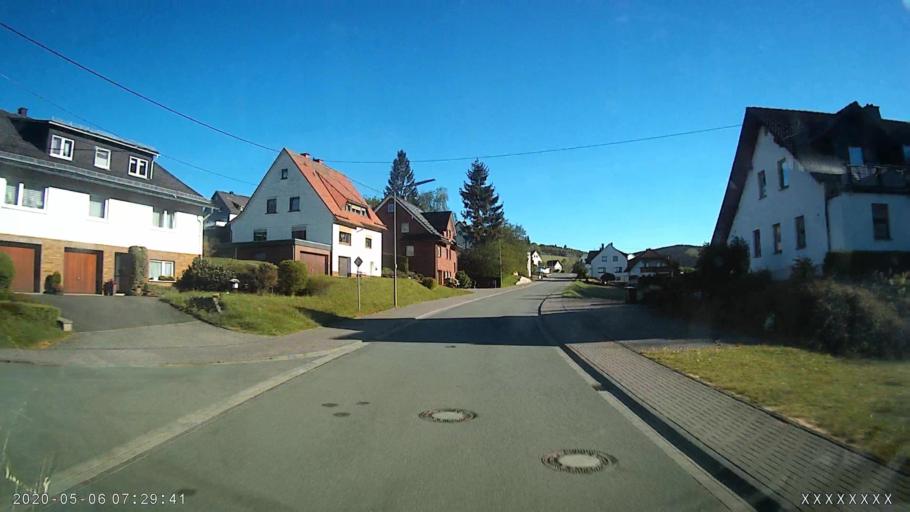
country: DE
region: Hesse
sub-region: Regierungsbezirk Giessen
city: Haiger
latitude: 50.8073
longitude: 8.2019
